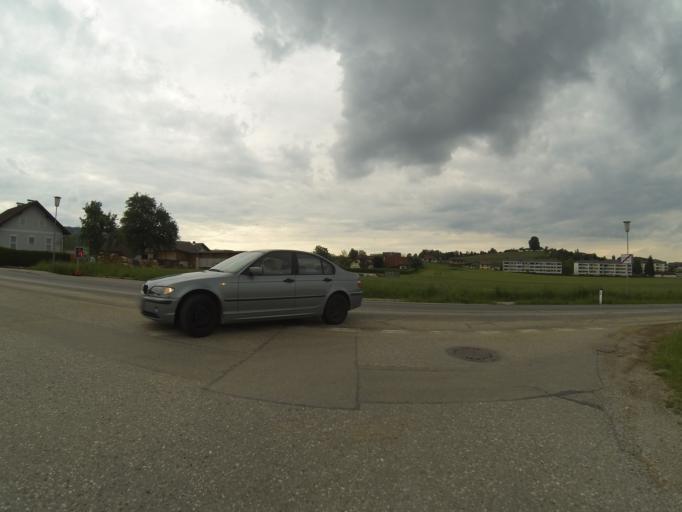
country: AT
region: Upper Austria
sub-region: Politischer Bezirk Gmunden
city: Altmunster
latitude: 47.9313
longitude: 13.7609
